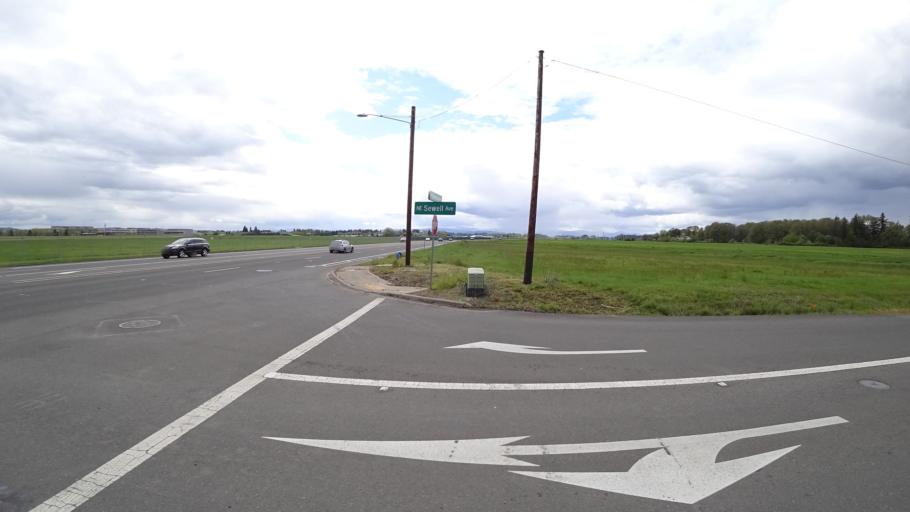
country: US
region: Oregon
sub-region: Washington County
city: Hillsboro
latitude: 45.5514
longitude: -122.9528
